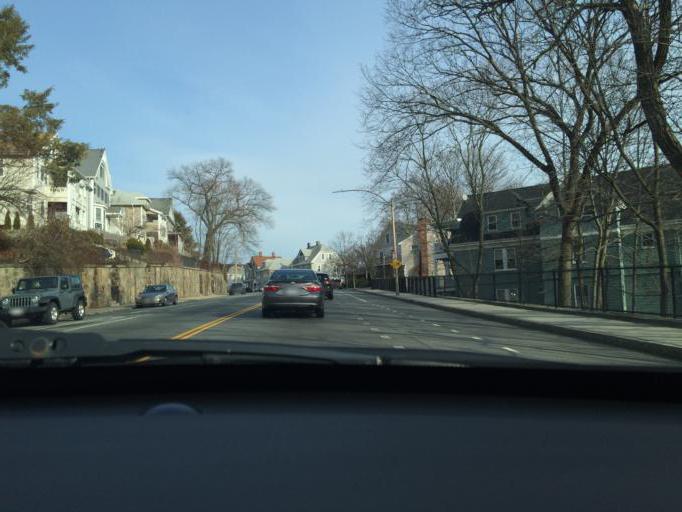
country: US
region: Massachusetts
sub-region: Suffolk County
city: Jamaica Plain
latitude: 42.2883
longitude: -71.1444
